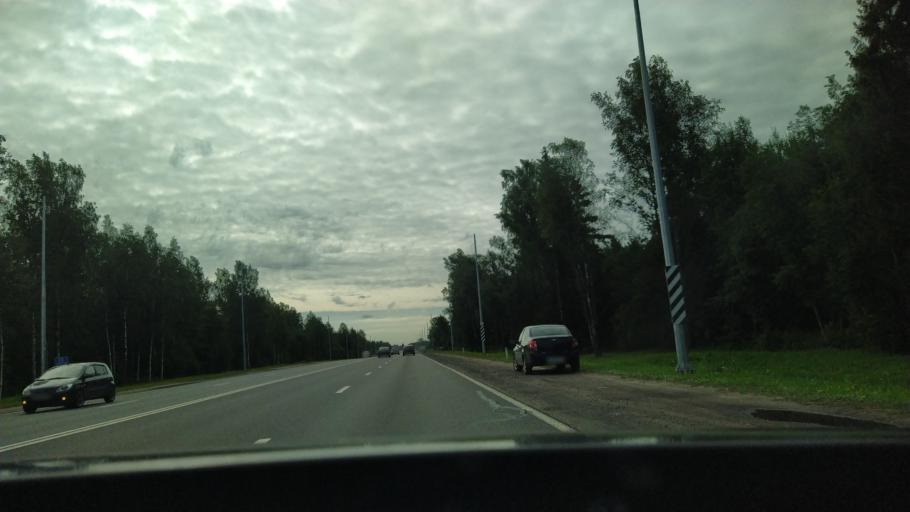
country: RU
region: Leningrad
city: Tosno
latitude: 59.5769
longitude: 30.8117
